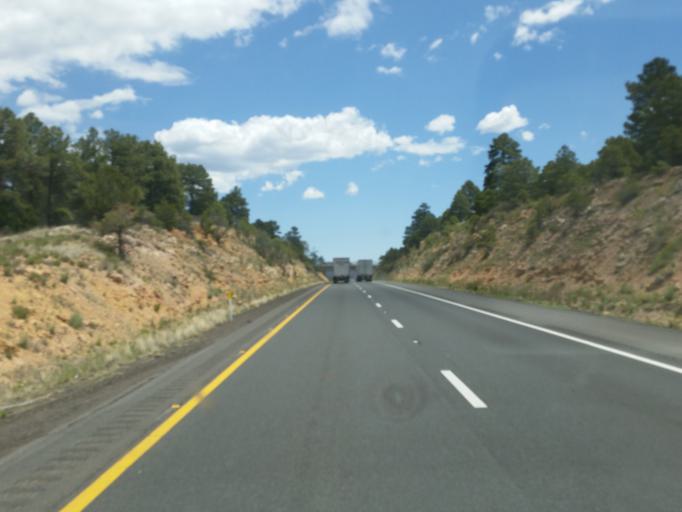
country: US
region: Arizona
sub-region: Coconino County
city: Flagstaff
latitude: 35.1994
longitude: -111.6111
